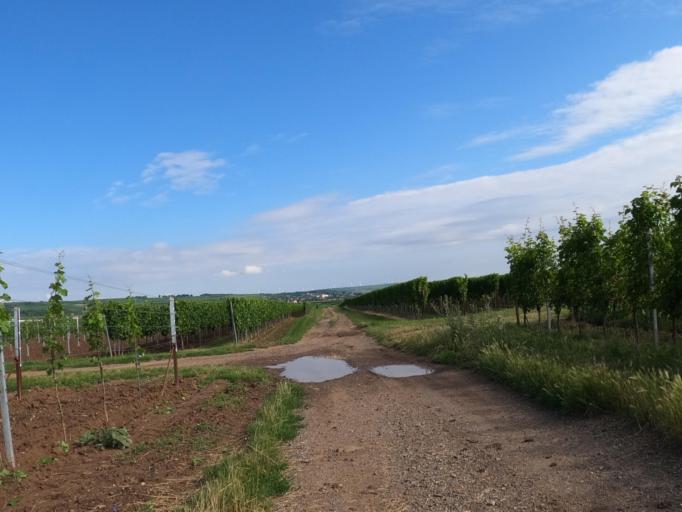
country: DE
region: Rheinland-Pfalz
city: Kirchheim an der Weinstrasse
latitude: 49.5322
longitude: 8.1678
